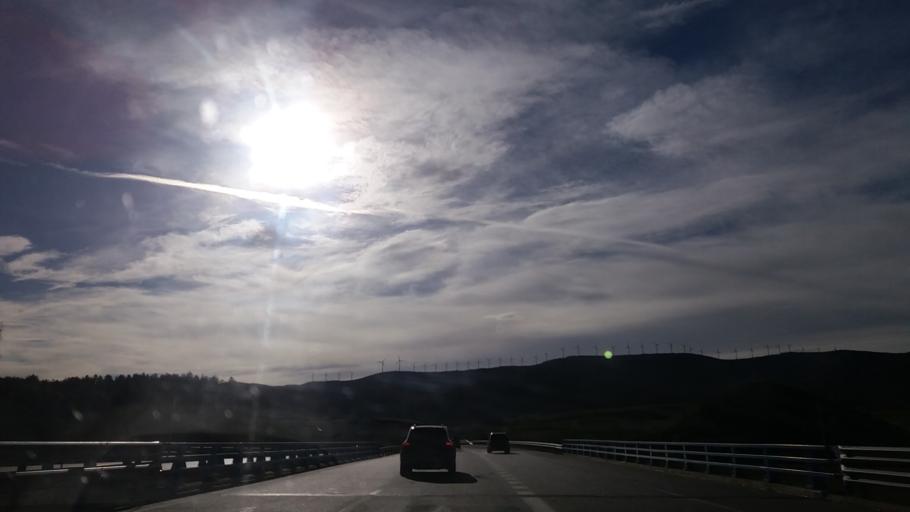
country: ES
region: Navarre
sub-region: Provincia de Navarra
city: Monreal
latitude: 42.6907
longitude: -1.4793
